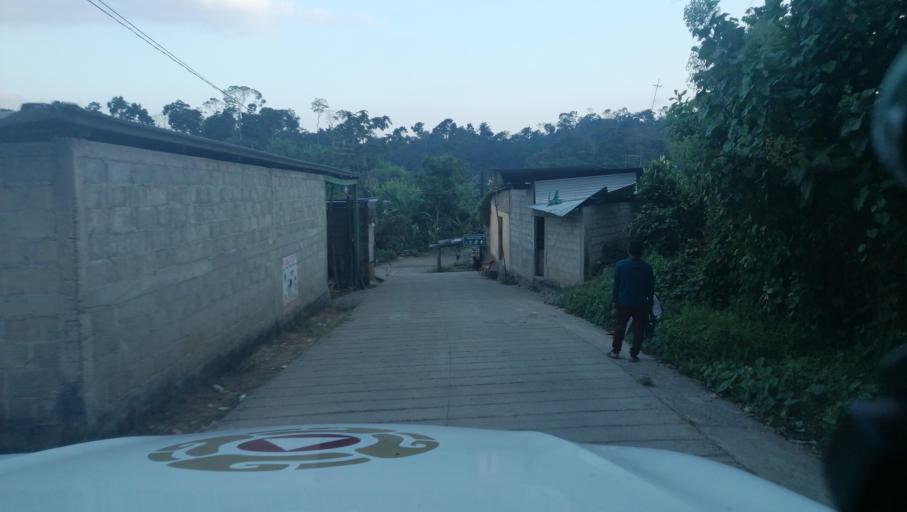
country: MX
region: Chiapas
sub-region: Cacahoatan
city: Benito Juarez
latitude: 15.0795
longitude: -92.2237
